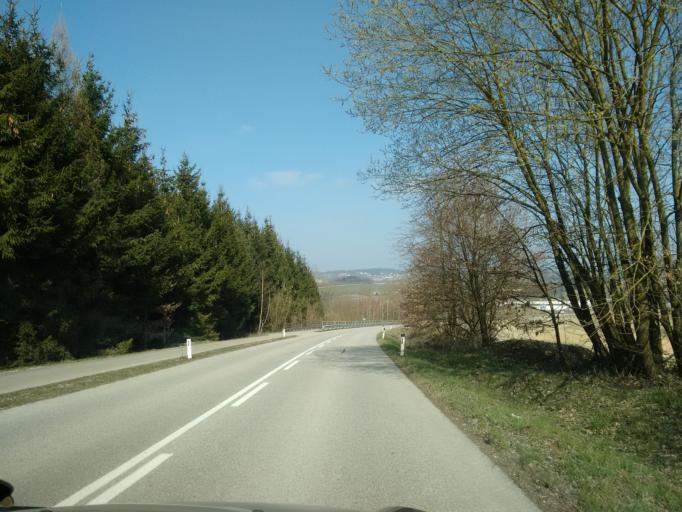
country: AT
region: Upper Austria
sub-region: Politischer Bezirk Grieskirchen
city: Bad Schallerbach
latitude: 48.2074
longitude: 13.9676
